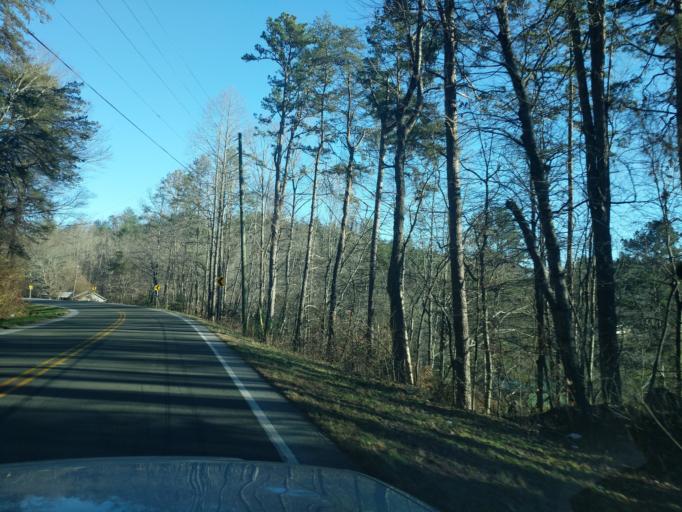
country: US
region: Georgia
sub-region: Rabun County
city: Clayton
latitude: 34.8445
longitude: -83.3510
